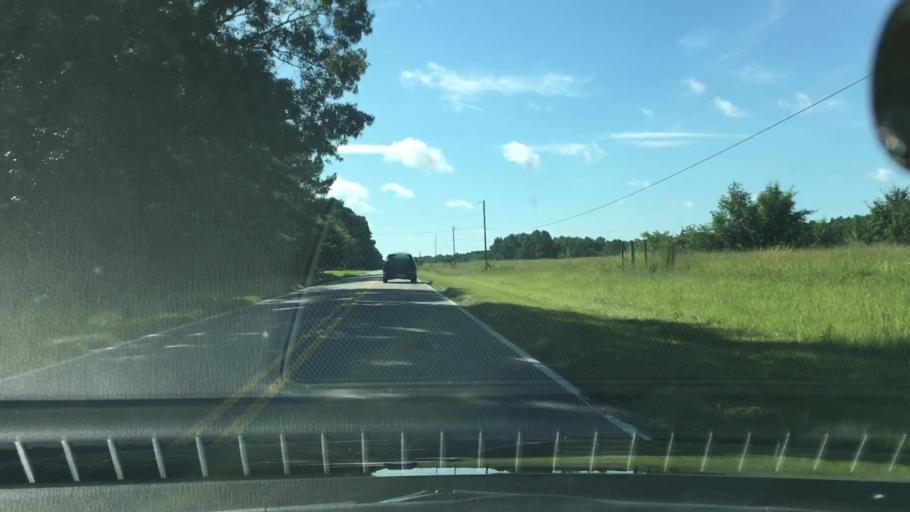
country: US
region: Georgia
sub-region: Putnam County
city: Jefferson
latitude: 33.3959
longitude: -83.2701
